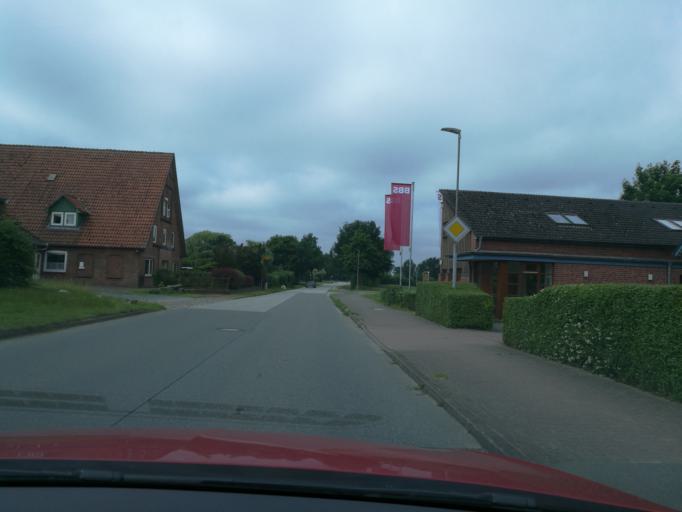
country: DE
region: Schleswig-Holstein
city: Lasbek
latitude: 53.7443
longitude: 10.3753
